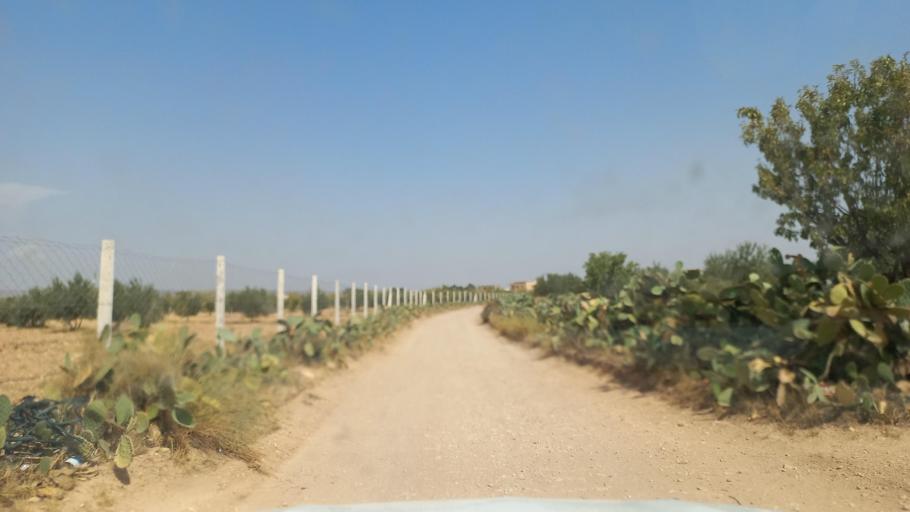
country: TN
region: Al Qasrayn
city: Kasserine
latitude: 35.2489
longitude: 9.0184
